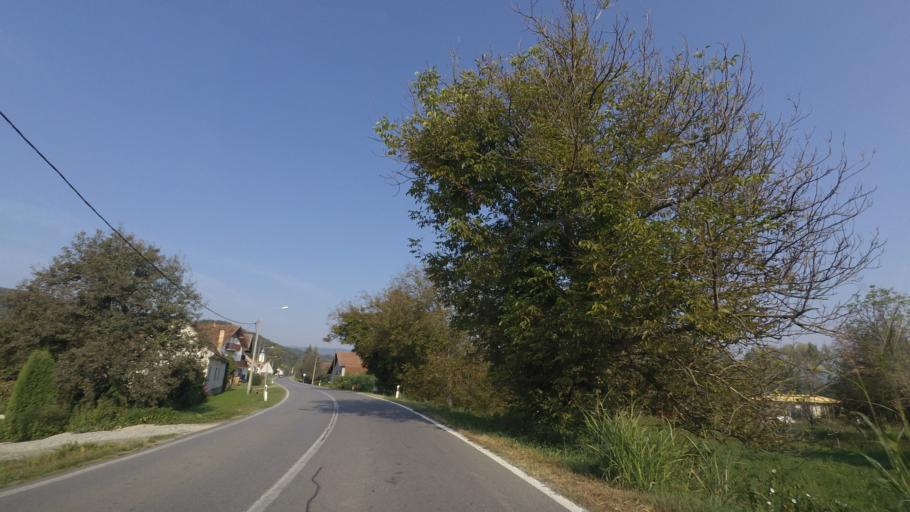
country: HR
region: Brodsko-Posavska
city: Resetari
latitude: 45.3653
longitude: 17.5342
